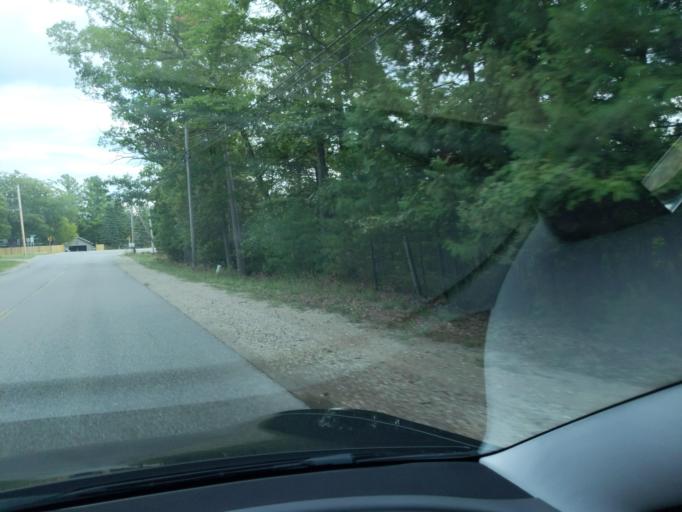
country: US
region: Michigan
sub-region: Kalkaska County
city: Rapid City
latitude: 44.8468
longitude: -85.3081
